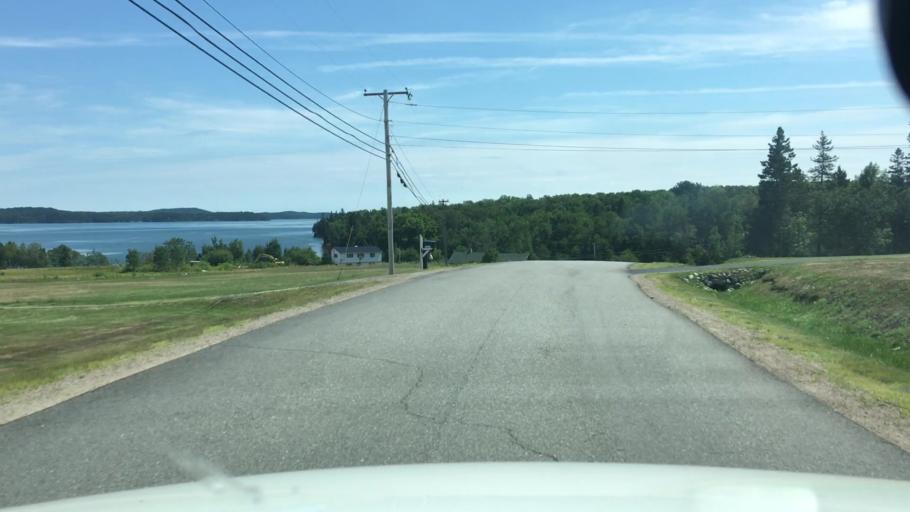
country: CA
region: New Brunswick
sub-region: Charlotte County
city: Saint Andrews
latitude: 44.9955
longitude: -67.0663
